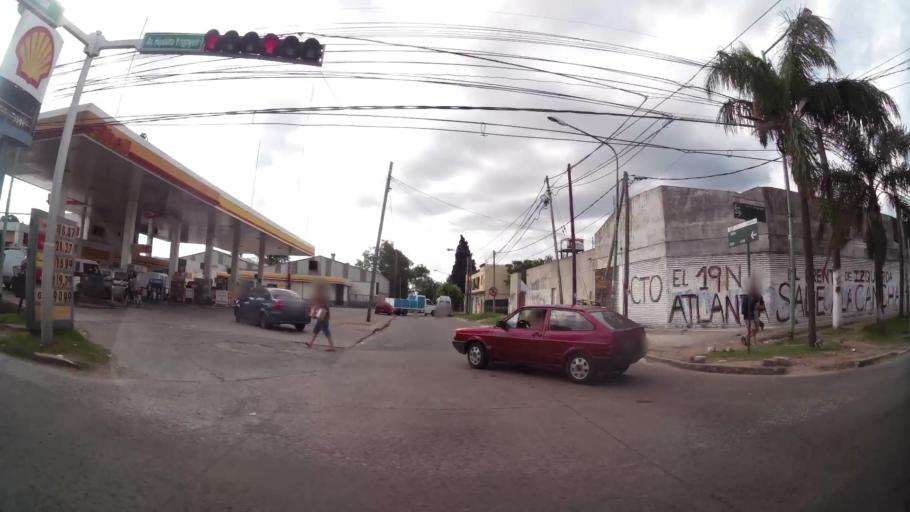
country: AR
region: Buenos Aires
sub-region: Partido de Tigre
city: Tigre
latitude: -34.4738
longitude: -58.6595
